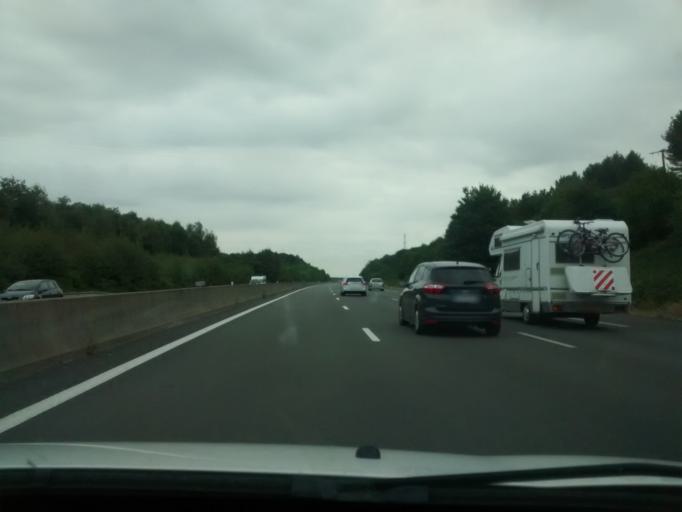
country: FR
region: Centre
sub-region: Departement d'Eure-et-Loir
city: Authon-du-Perche
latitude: 48.2007
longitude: 0.8821
